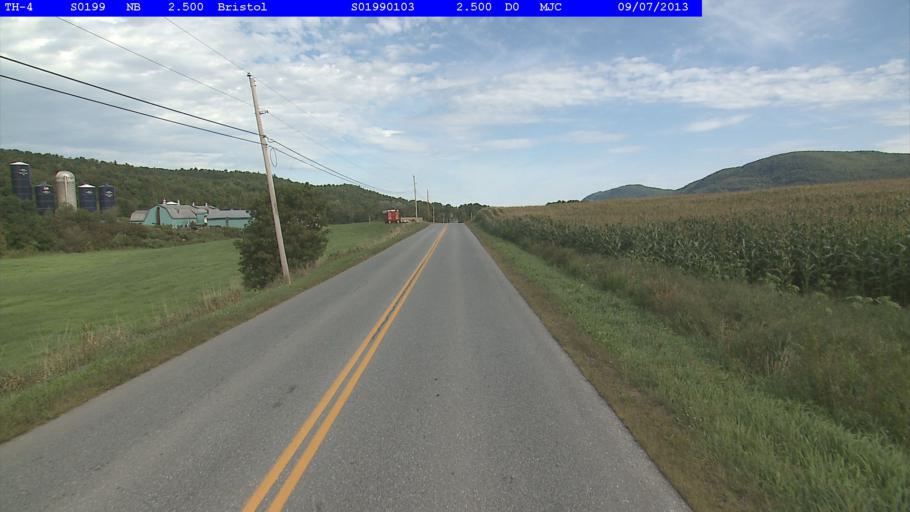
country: US
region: Vermont
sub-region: Addison County
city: Bristol
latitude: 44.1642
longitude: -73.1002
